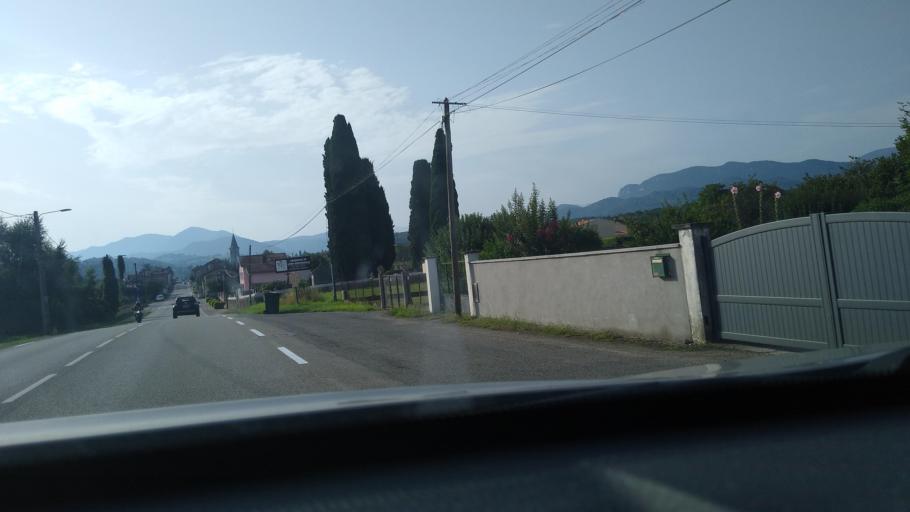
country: FR
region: Midi-Pyrenees
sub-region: Departement de l'Ariege
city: Saint-Lizier
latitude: 43.0114
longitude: 1.1156
